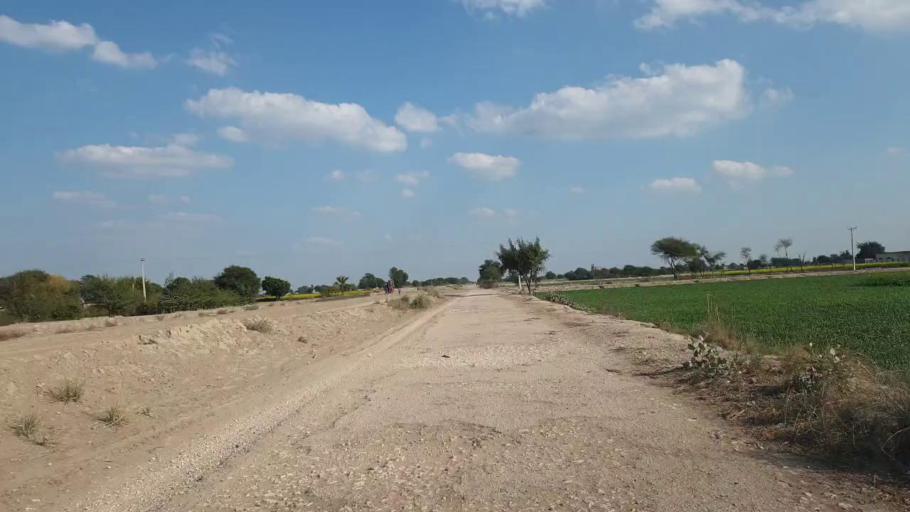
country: PK
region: Sindh
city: Shahpur Chakar
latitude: 26.1056
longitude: 68.5813
